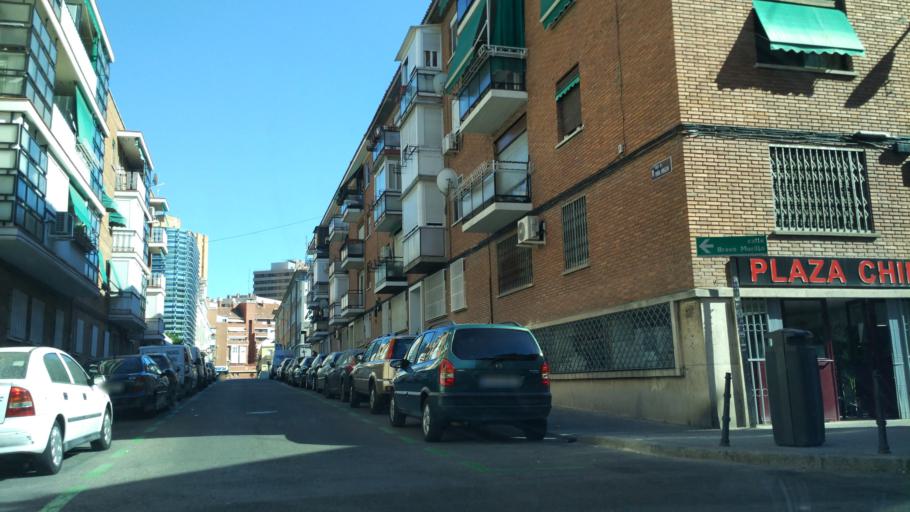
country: ES
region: Madrid
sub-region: Provincia de Madrid
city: Chamartin
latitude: 40.4664
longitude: -3.6948
